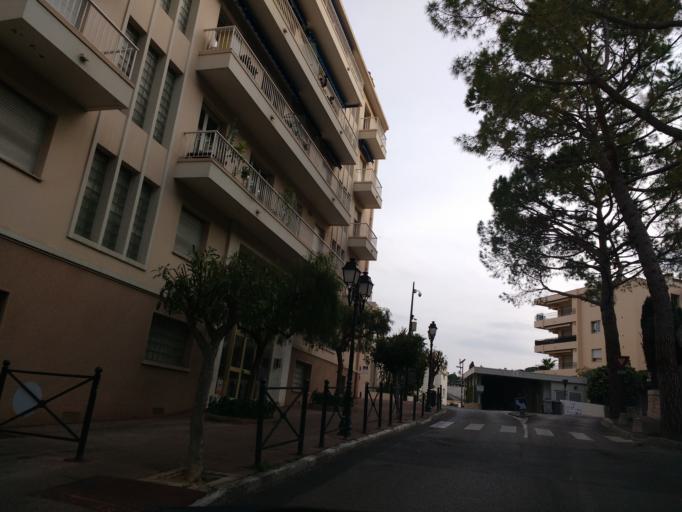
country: FR
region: Provence-Alpes-Cote d'Azur
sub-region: Departement des Alpes-Maritimes
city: Beaulieu-sur-Mer
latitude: 43.7081
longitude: 7.3294
